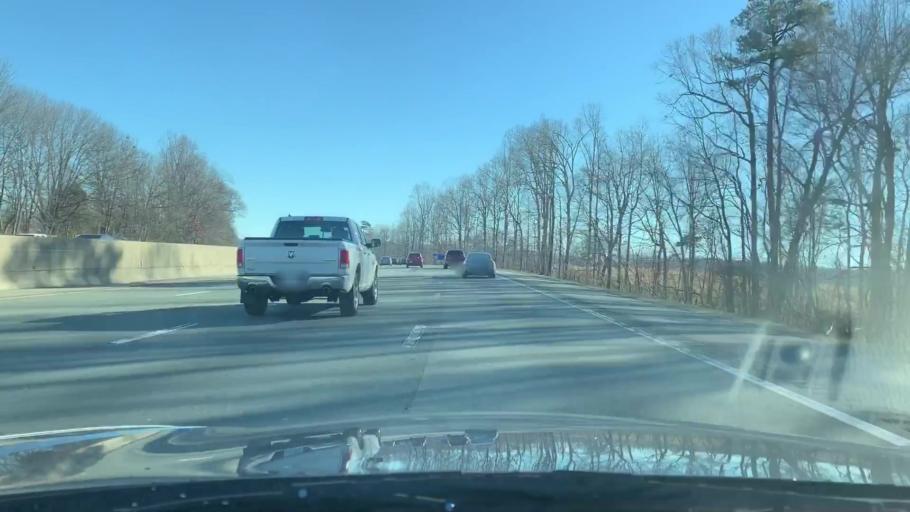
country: US
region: North Carolina
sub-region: Alamance County
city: Haw River
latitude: 36.0657
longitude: -79.3218
